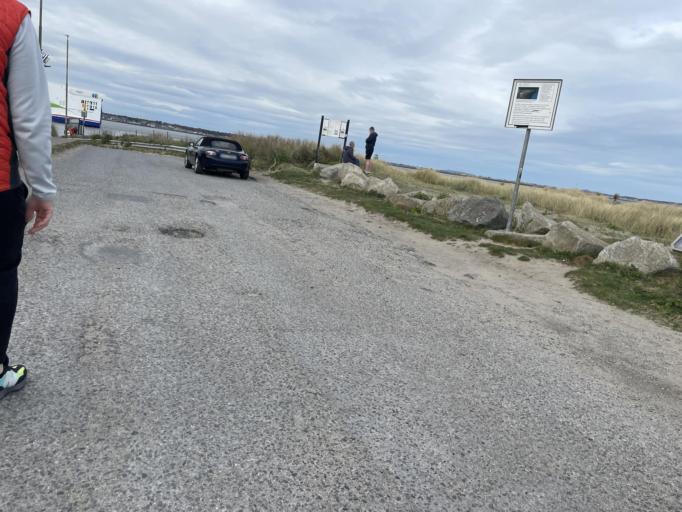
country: IE
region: Leinster
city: Dollymount
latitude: 53.3403
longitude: -6.1798
